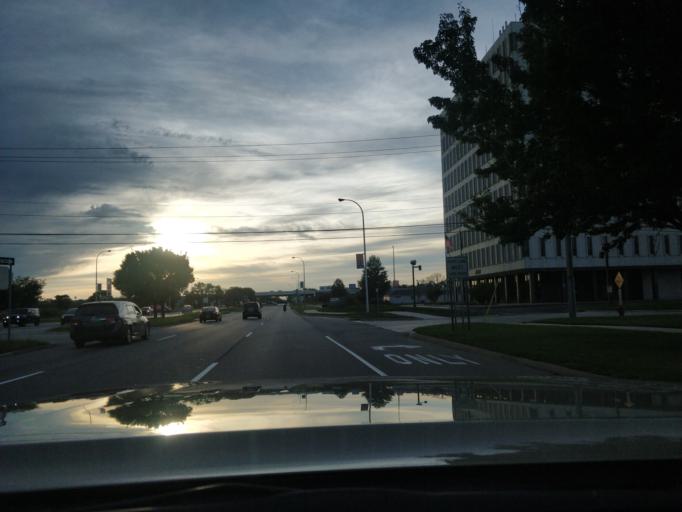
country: US
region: Michigan
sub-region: Wayne County
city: Southgate
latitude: 42.1985
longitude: -83.2355
